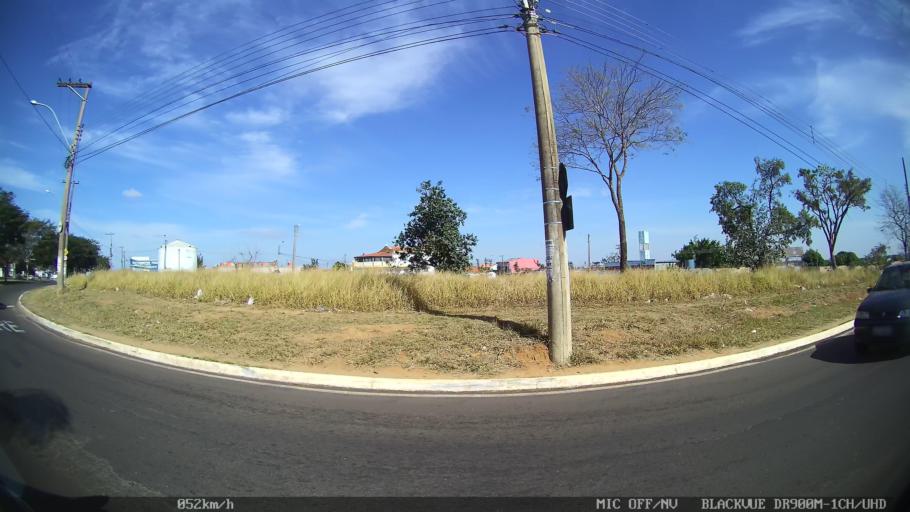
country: BR
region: Sao Paulo
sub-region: Franca
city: Franca
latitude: -20.4811
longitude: -47.4040
